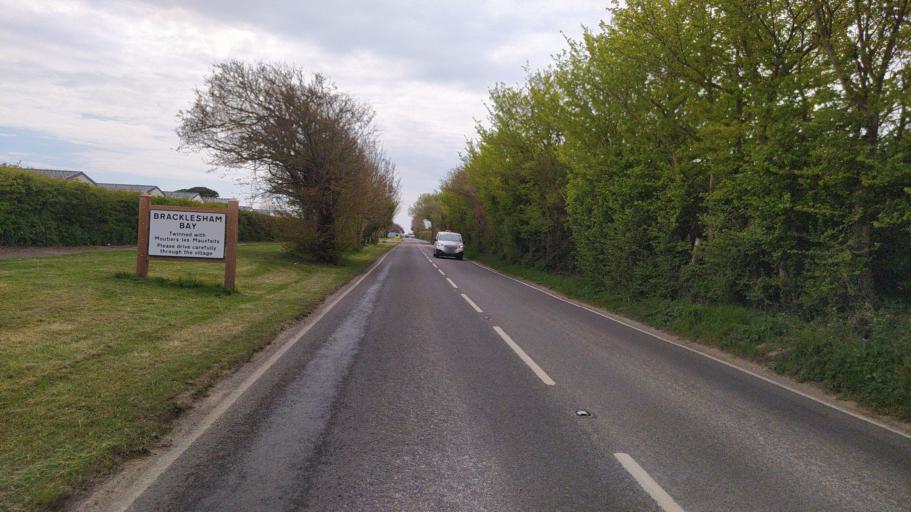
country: GB
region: England
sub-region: West Sussex
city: East Wittering
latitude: 50.7702
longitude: -0.8536
